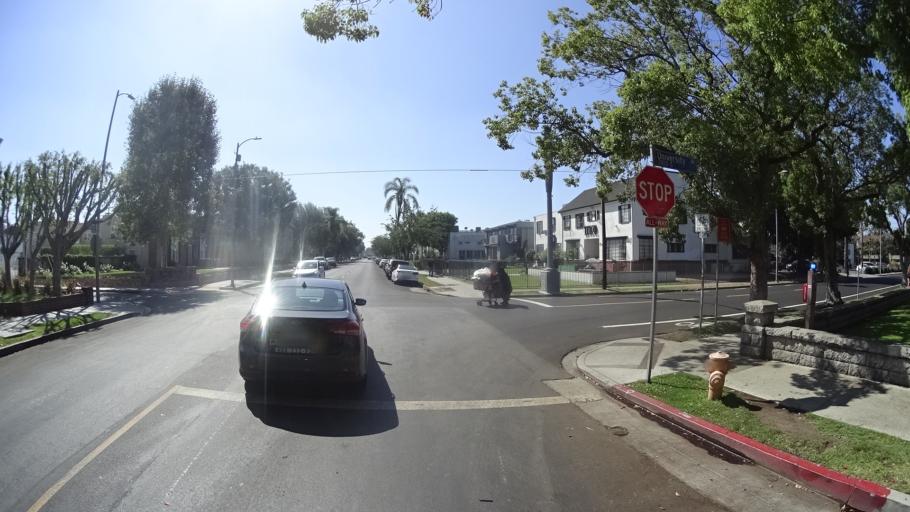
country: US
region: California
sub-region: Los Angeles County
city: Los Angeles
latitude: 34.0278
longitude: -118.2813
